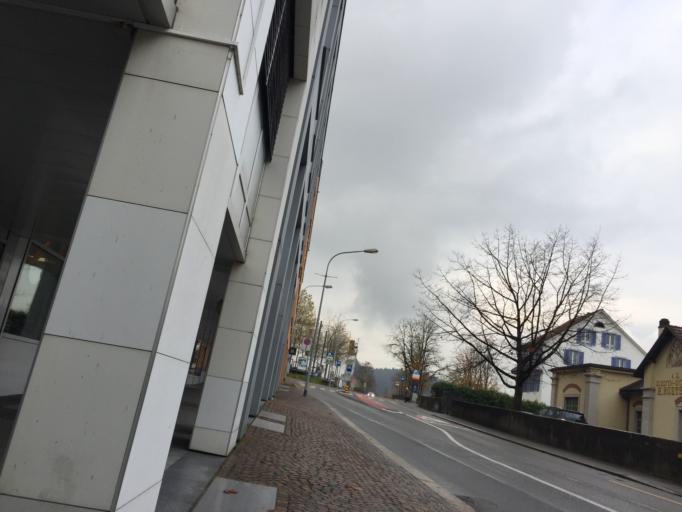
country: CH
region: Aargau
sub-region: Bezirk Aarau
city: Aarau
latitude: 47.3899
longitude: 8.0435
